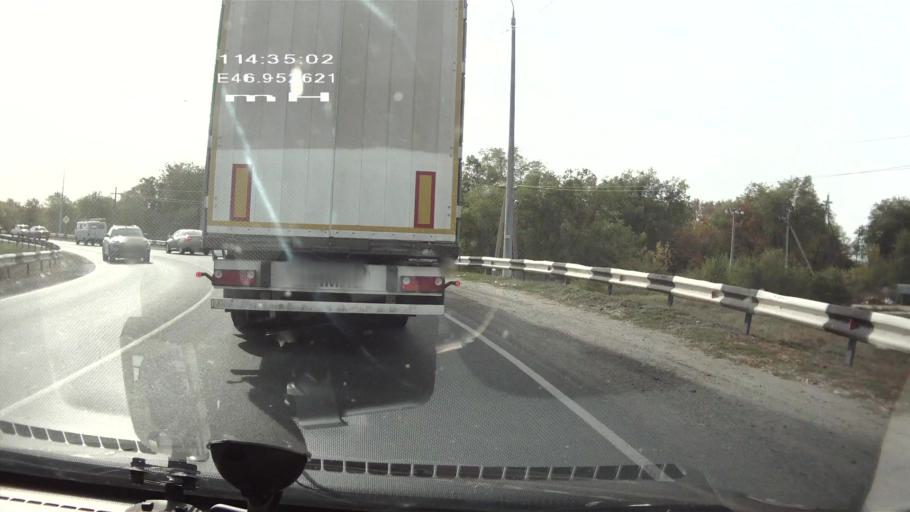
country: RU
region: Saratov
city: Sennoy
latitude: 52.1540
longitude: 46.9532
